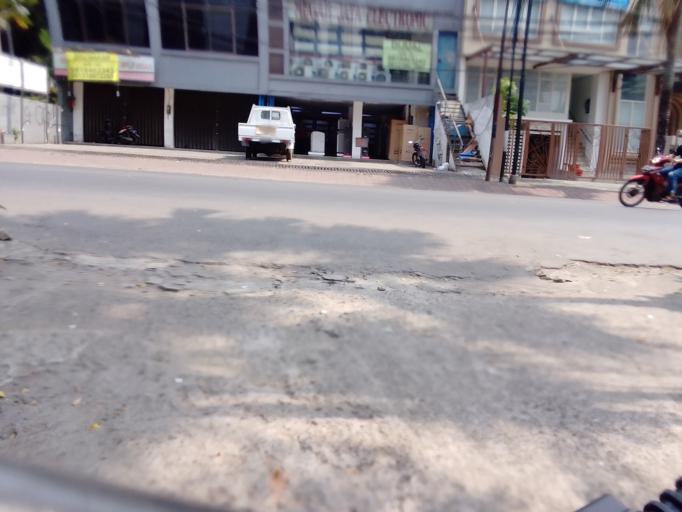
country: ID
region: Jakarta Raya
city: Jakarta
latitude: -6.2073
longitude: 106.8107
